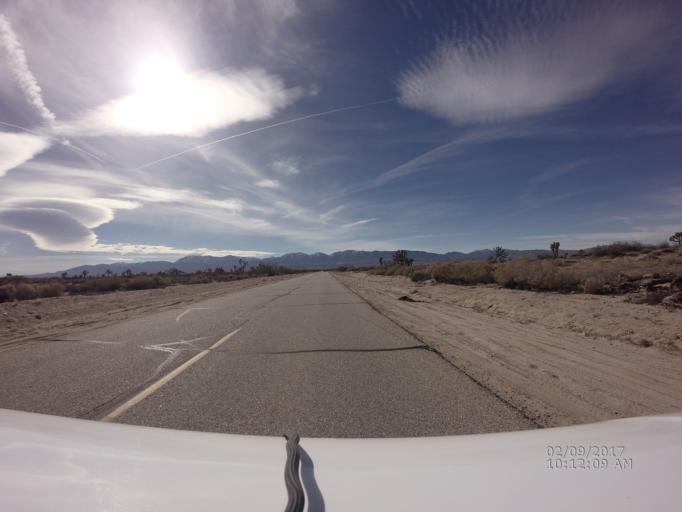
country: US
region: California
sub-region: Los Angeles County
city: Lake Los Angeles
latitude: 34.5775
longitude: -117.8897
